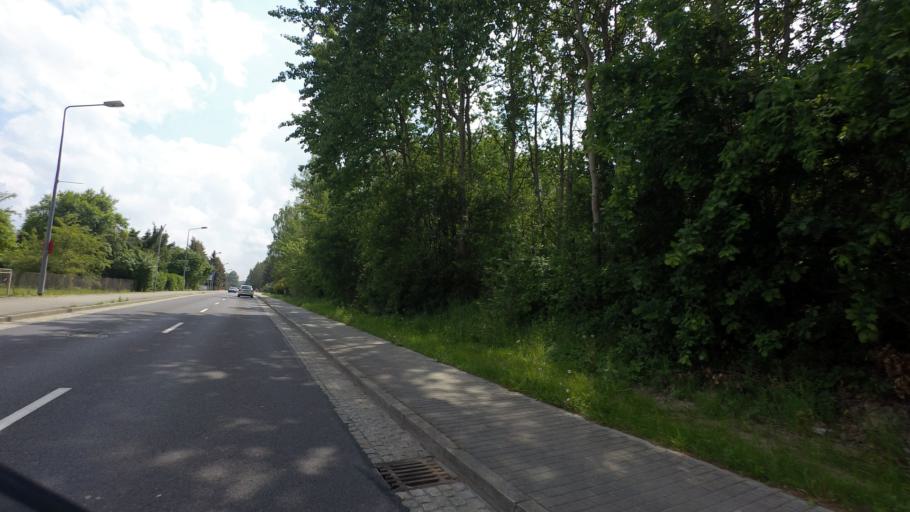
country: DE
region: Saxony
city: Weisswasser
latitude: 51.5172
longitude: 14.6082
